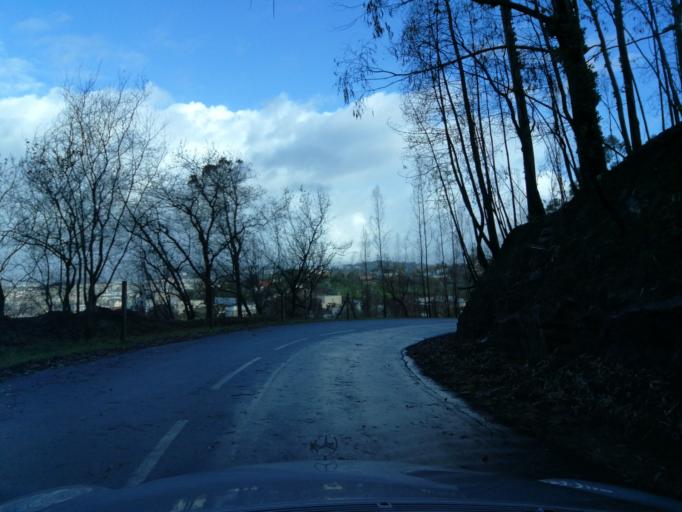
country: PT
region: Braga
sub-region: Braga
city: Braga
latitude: 41.5406
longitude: -8.3901
